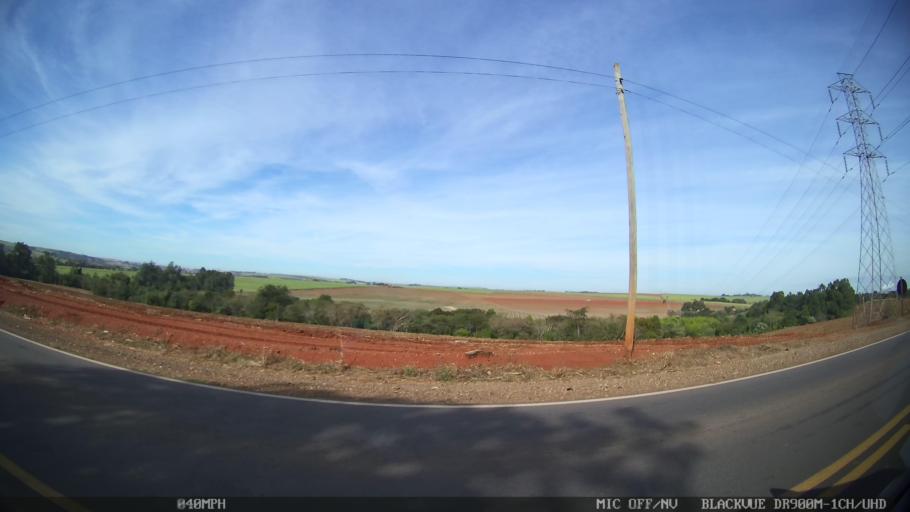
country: BR
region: Sao Paulo
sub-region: Rio Das Pedras
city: Rio das Pedras
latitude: -22.7895
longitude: -47.6388
